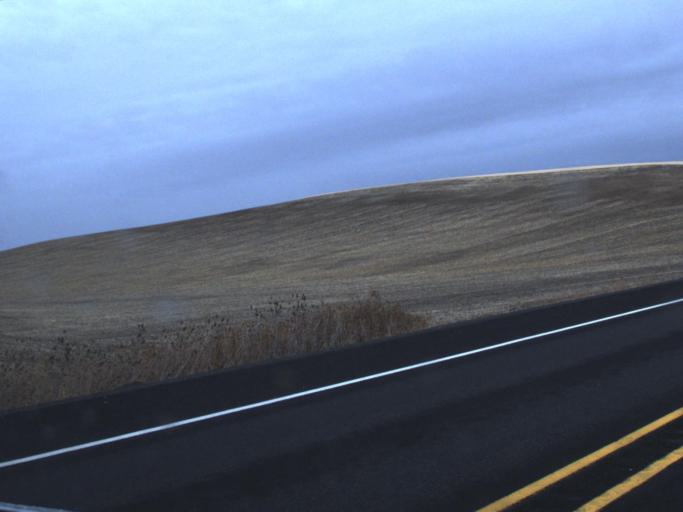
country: US
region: Washington
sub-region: Whitman County
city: Pullman
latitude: 46.6297
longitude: -117.1738
